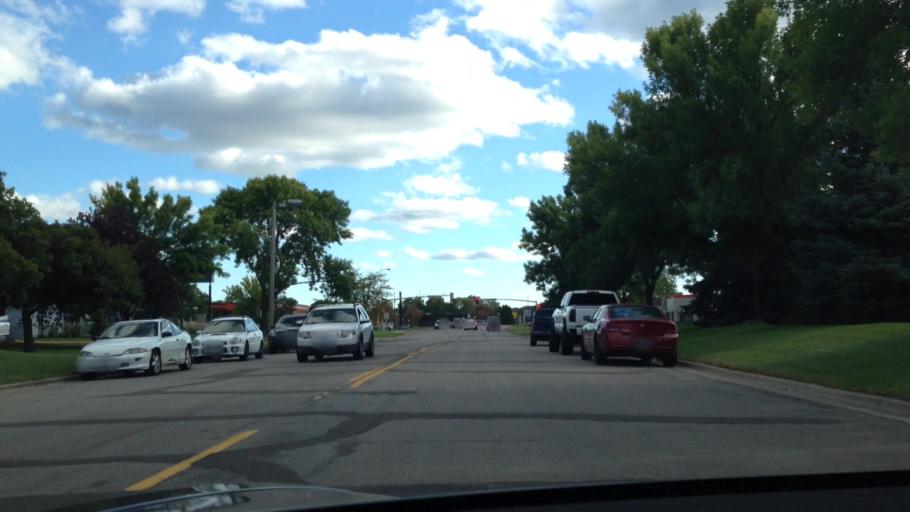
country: US
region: Minnesota
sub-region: Hennepin County
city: Osseo
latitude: 45.1106
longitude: -93.3871
